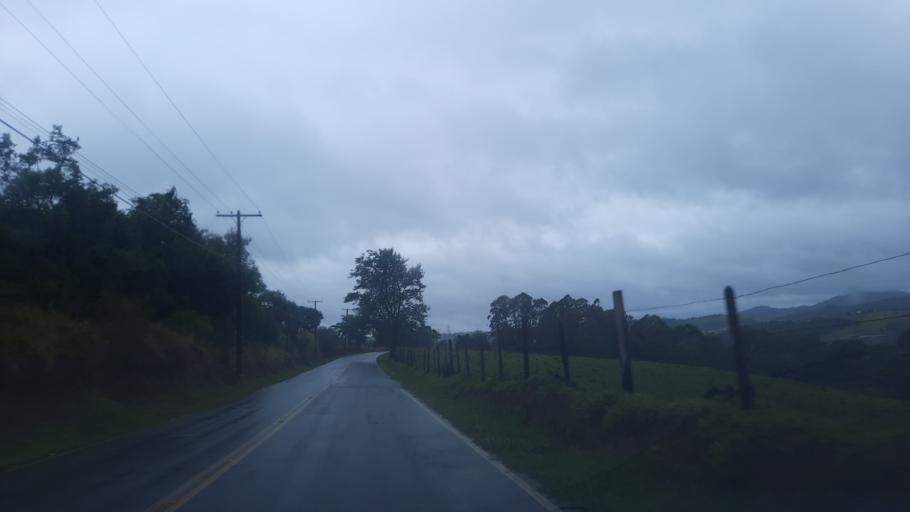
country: BR
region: Sao Paulo
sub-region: Atibaia
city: Atibaia
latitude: -23.0742
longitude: -46.5187
